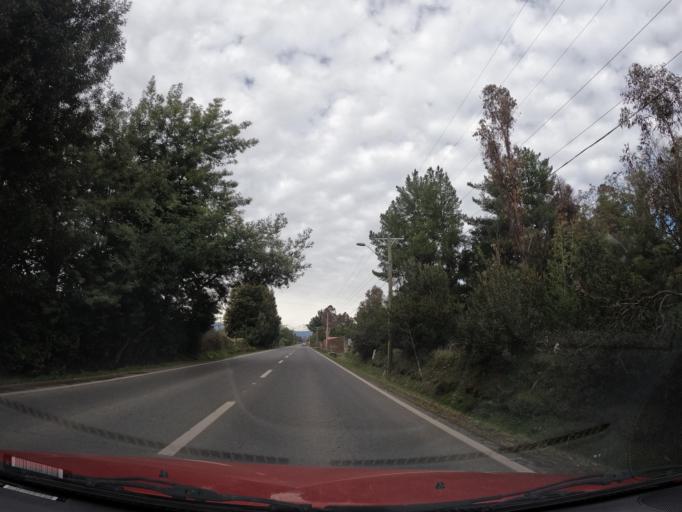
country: CL
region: Maule
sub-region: Provincia de Linares
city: Linares
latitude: -35.8916
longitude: -71.5256
